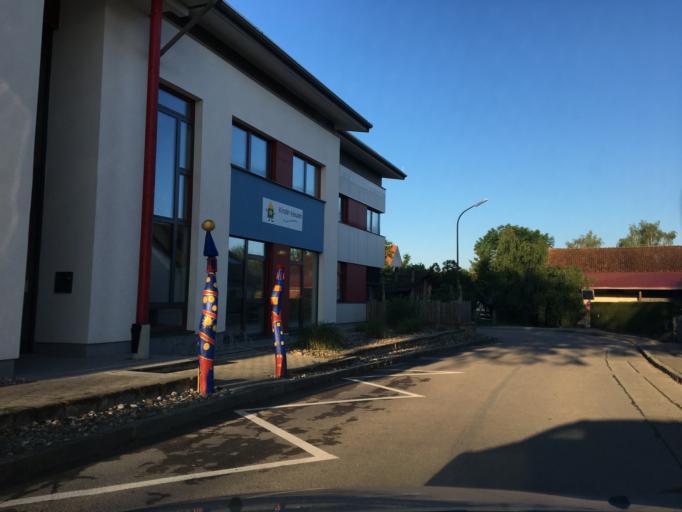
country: DE
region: Bavaria
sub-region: Upper Bavaria
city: Haimhausen
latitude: 48.3198
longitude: 11.5559
